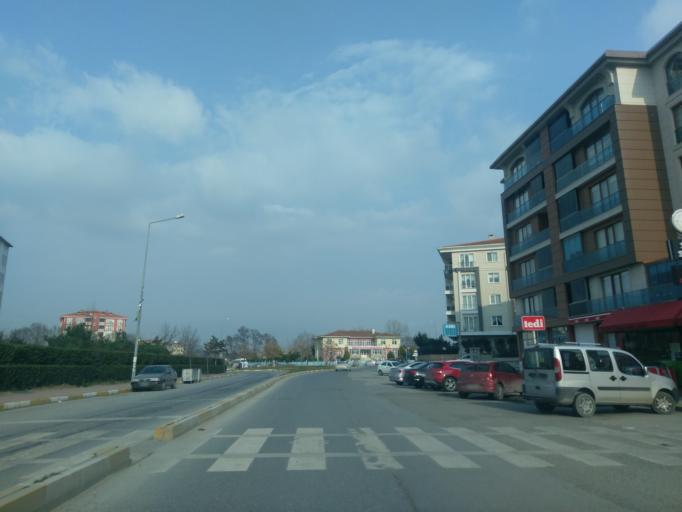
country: TR
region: Istanbul
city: Silivri
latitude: 41.0823
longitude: 28.2615
